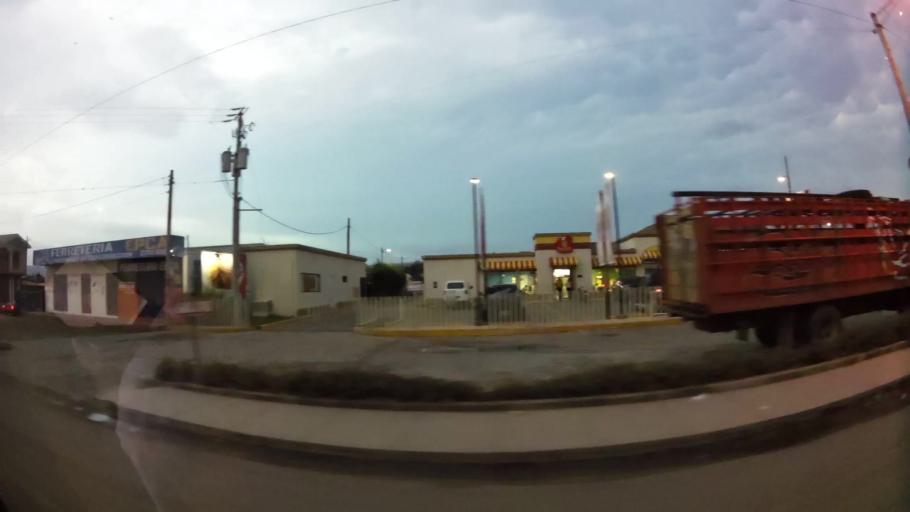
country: NI
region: Esteli
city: Esteli
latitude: 13.0963
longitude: -86.3512
